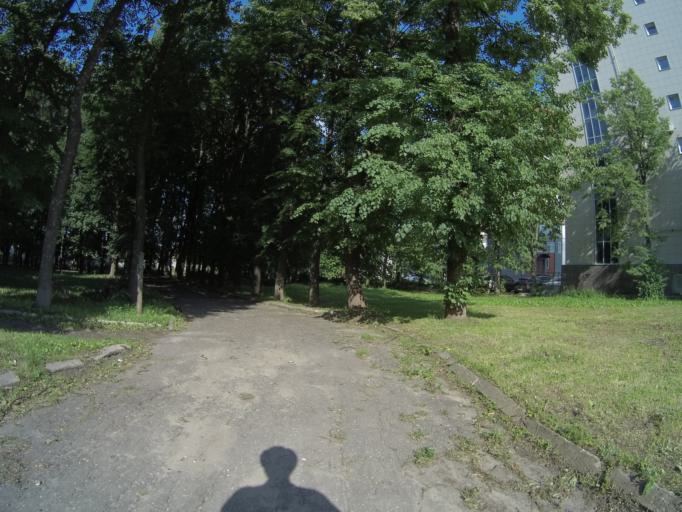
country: RU
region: Vladimir
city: Vladimir
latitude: 56.1439
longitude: 40.3915
